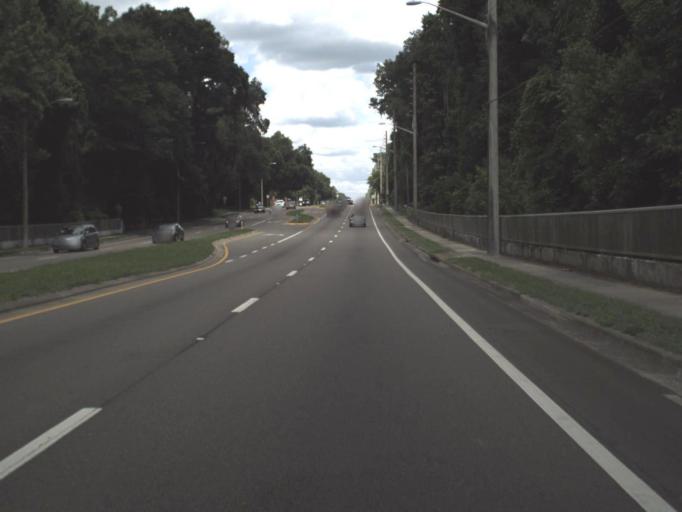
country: US
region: Florida
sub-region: Alachua County
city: Gainesville
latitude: 29.6886
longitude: -82.3819
